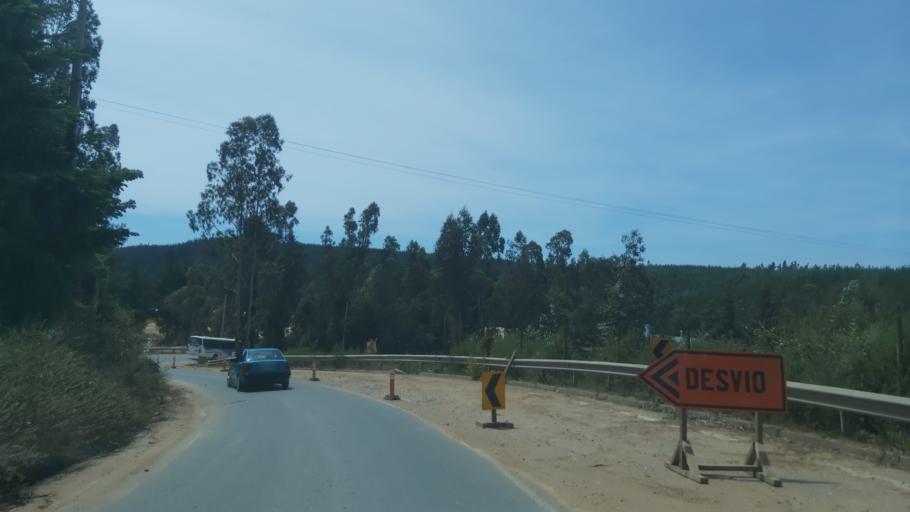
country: CL
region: Maule
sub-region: Provincia de Talca
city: Constitucion
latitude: -35.3879
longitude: -72.4240
